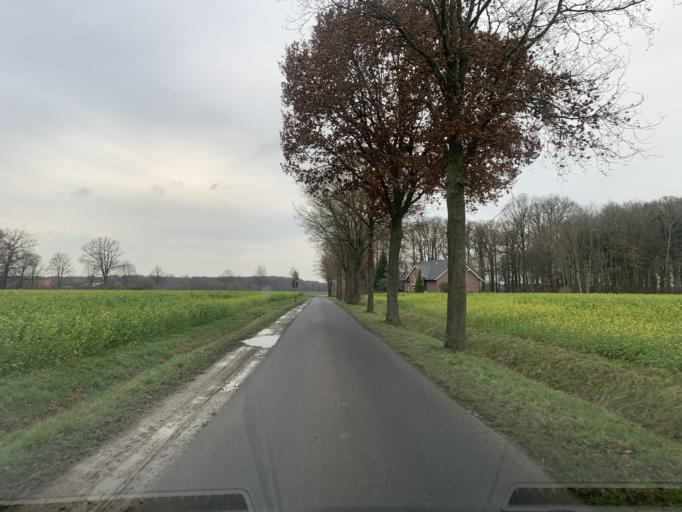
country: DE
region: North Rhine-Westphalia
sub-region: Regierungsbezirk Munster
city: Senden
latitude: 51.8907
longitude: 7.5666
